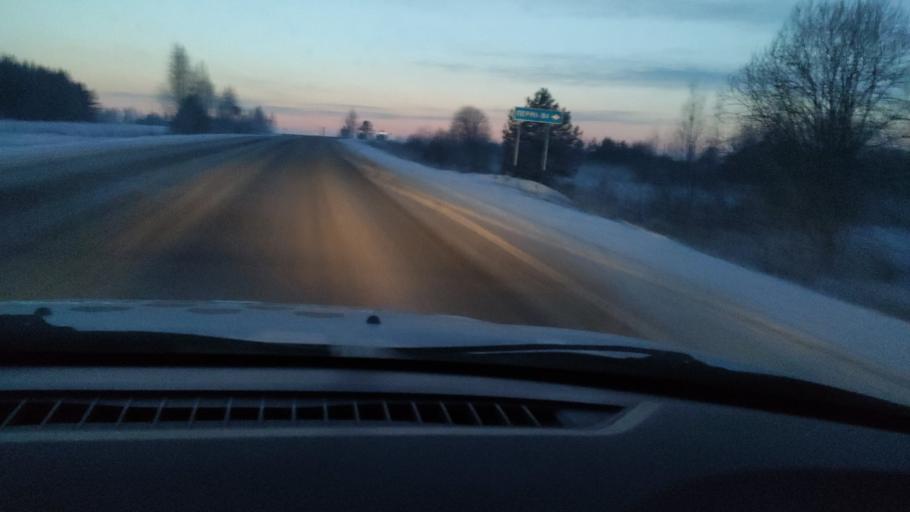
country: RU
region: Perm
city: Kungur
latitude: 57.4072
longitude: 56.8991
